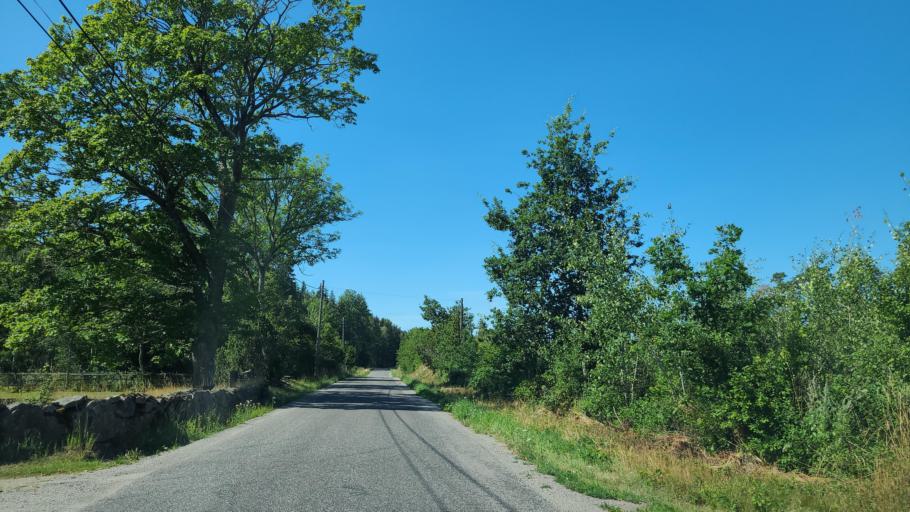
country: SE
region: Kalmar
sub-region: Kalmar Kommun
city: Ljungbyholm
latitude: 56.5698
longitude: 16.0673
